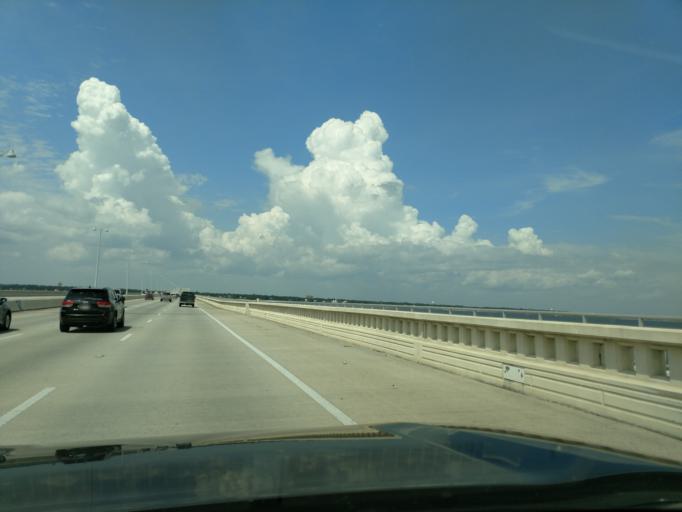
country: US
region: Mississippi
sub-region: Harrison County
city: Biloxi
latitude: 30.3936
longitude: -88.8563
